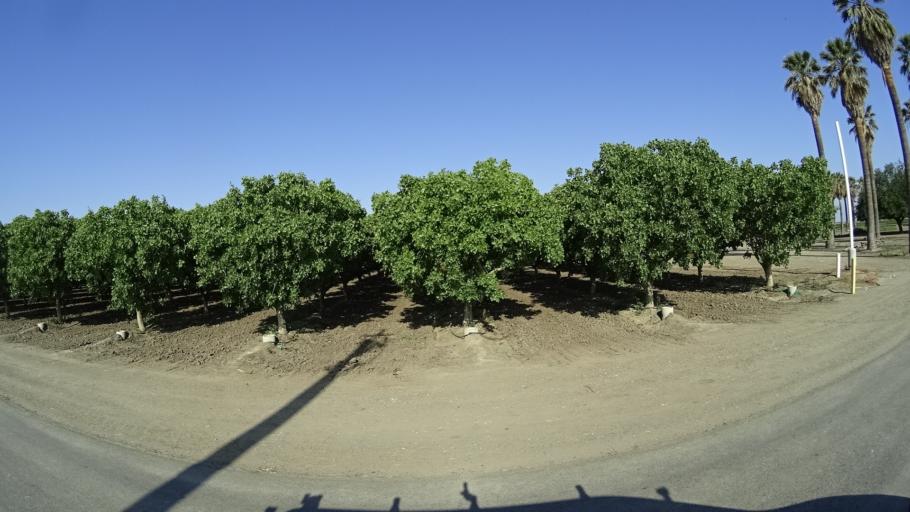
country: US
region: California
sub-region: Kings County
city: Home Garden
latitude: 36.2685
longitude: -119.5294
